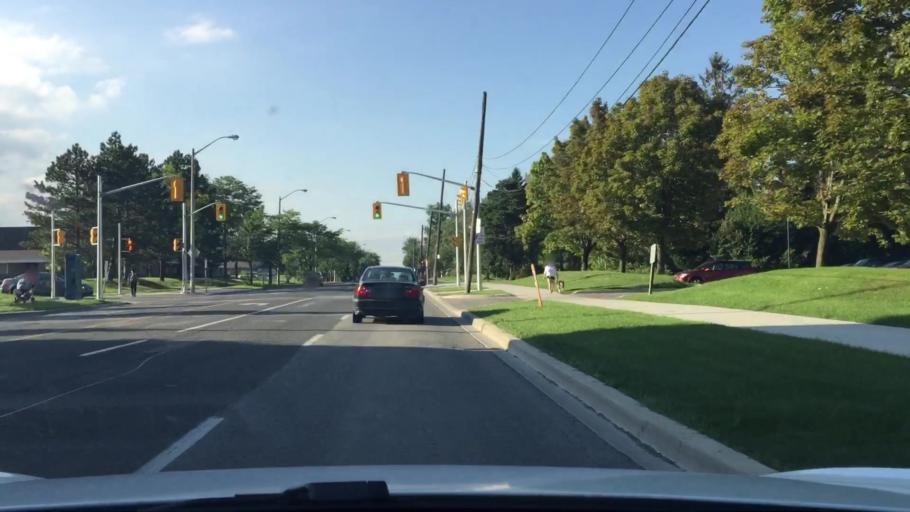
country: CA
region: Ontario
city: Scarborough
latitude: 43.8024
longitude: -79.3082
